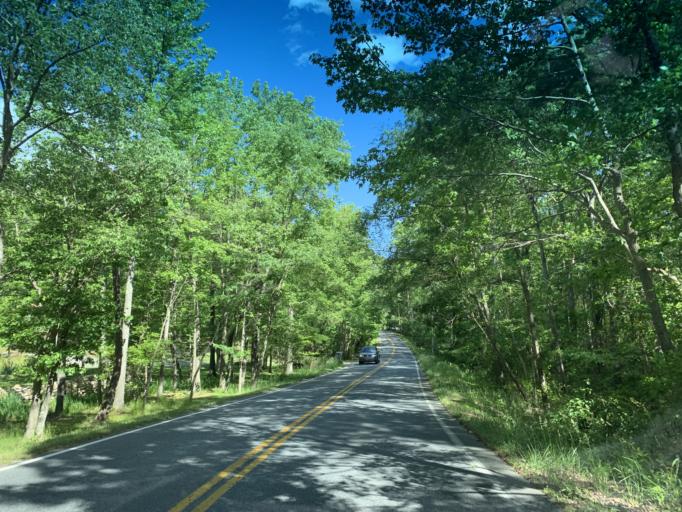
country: US
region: Maryland
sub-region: Cecil County
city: Charlestown
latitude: 39.5430
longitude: -75.9288
